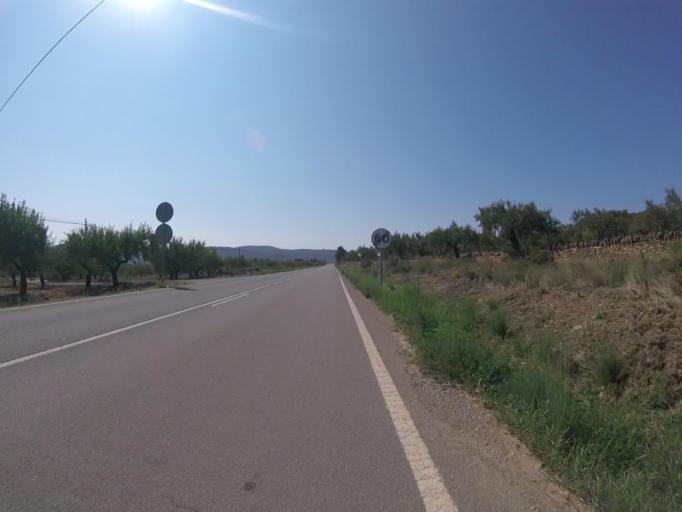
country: ES
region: Valencia
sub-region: Provincia de Castello
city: Adzaneta
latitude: 40.2336
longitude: -0.1773
